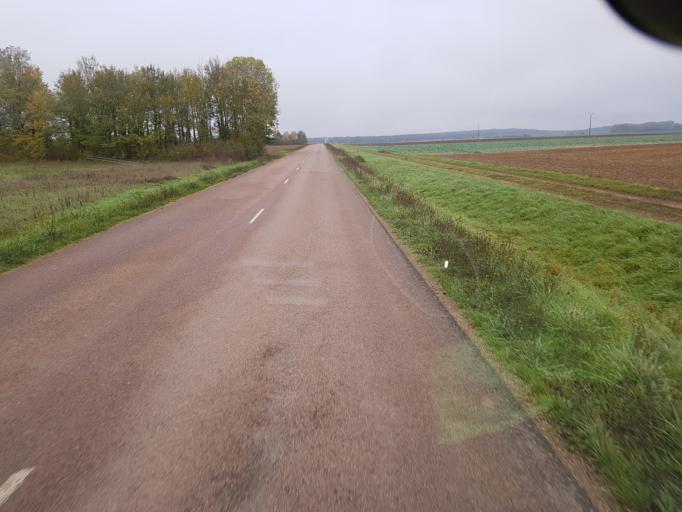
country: FR
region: Bourgogne
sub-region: Departement de la Cote-d'Or
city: Saint-Julien
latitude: 47.4242
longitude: 5.2084
